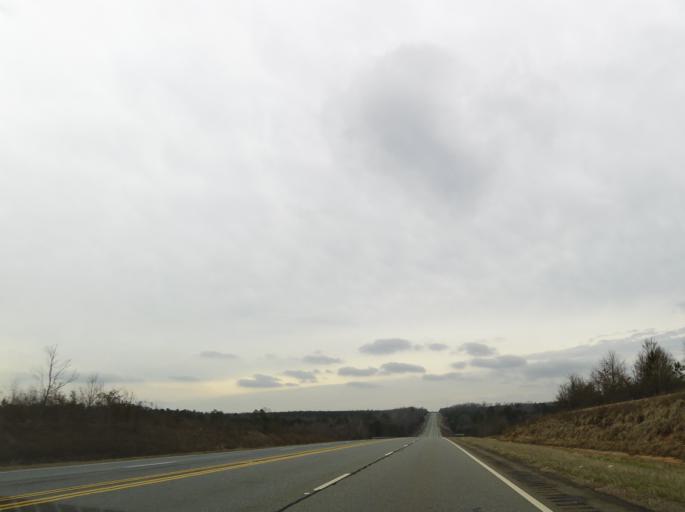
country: US
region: Georgia
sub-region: Bleckley County
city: Cochran
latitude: 32.4881
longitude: -83.3987
